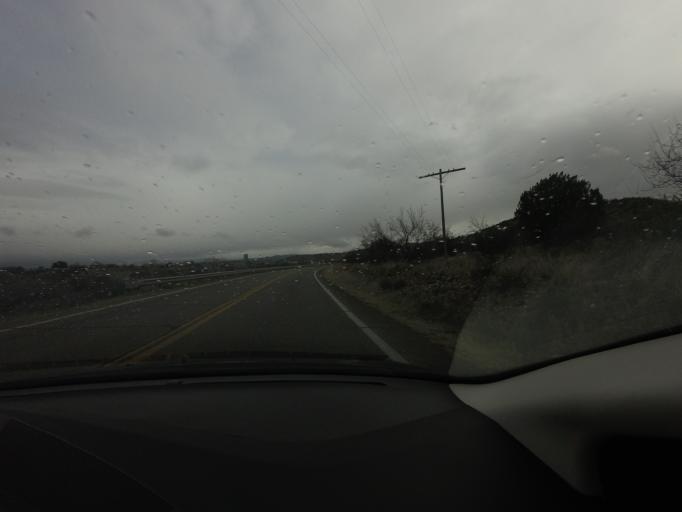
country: US
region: Arizona
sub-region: Yavapai County
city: Lake Montezuma
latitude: 34.6602
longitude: -111.8220
